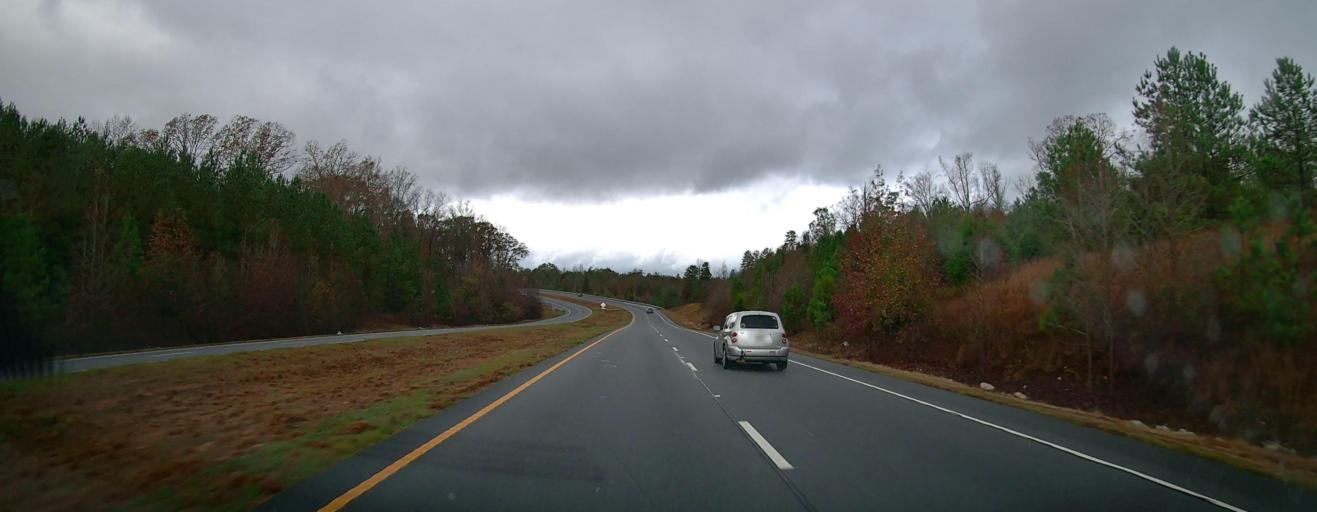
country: US
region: Georgia
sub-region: Jackson County
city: Nicholson
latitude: 34.0562
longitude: -83.4109
